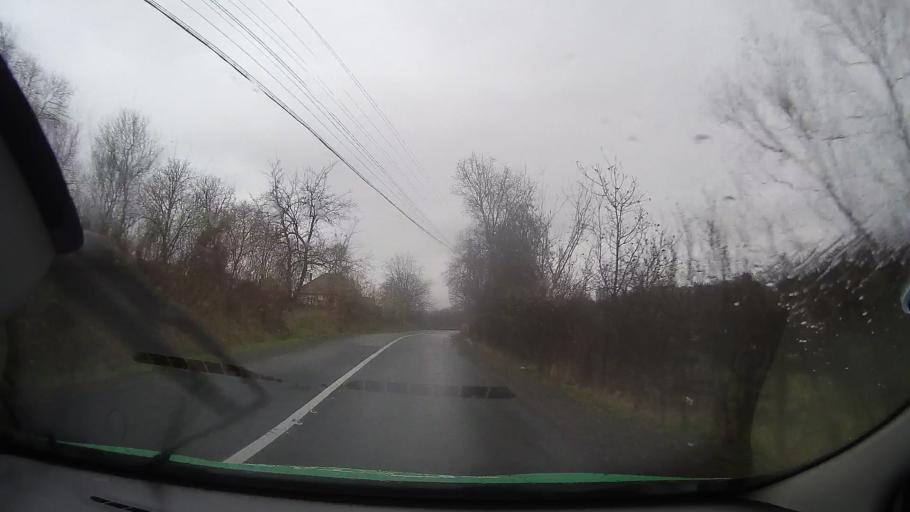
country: RO
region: Mures
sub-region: Comuna Vatava
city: Vatava
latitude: 46.9541
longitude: 24.7629
